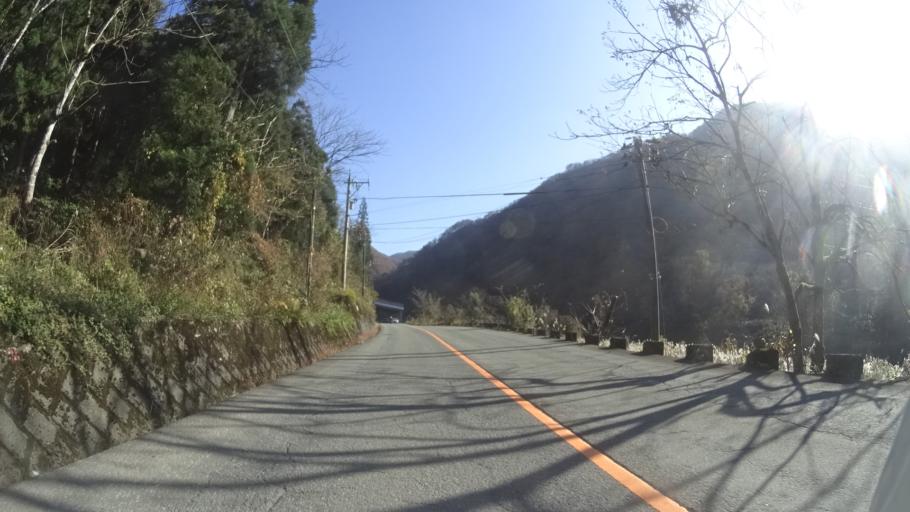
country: JP
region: Fukui
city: Ono
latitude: 35.9135
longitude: 136.6272
